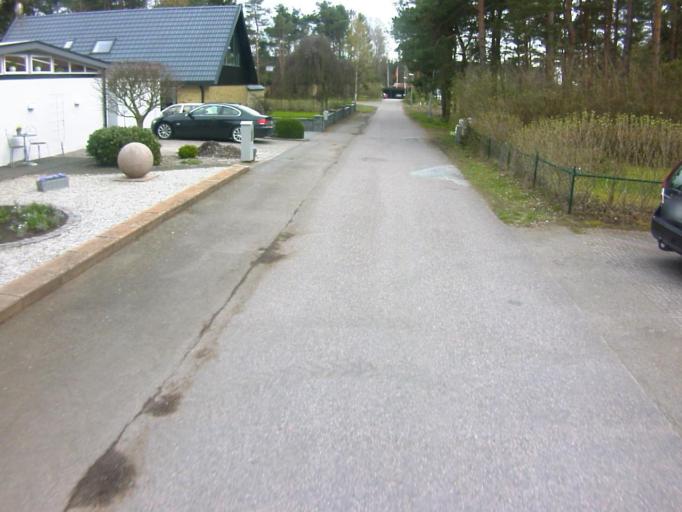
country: SE
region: Skane
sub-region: Kavlinge Kommun
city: Hofterup
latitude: 55.7941
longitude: 12.9675
